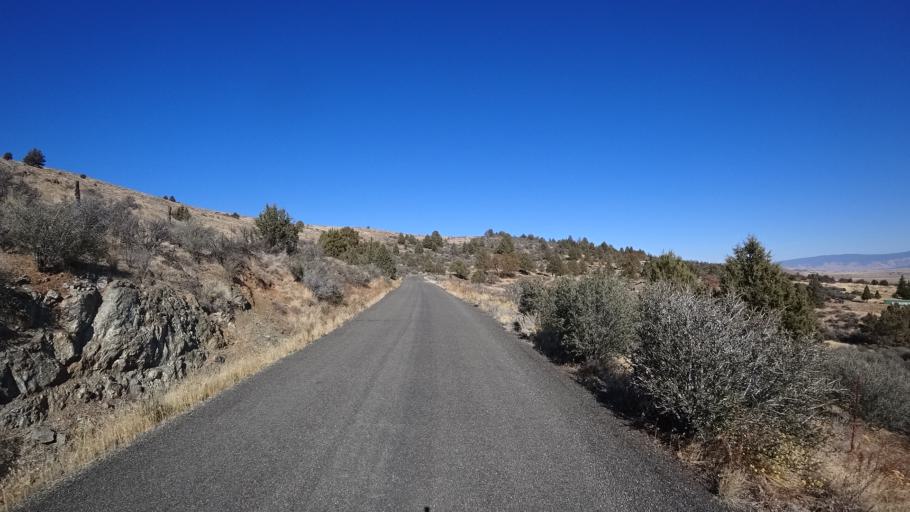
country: US
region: California
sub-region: Siskiyou County
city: Yreka
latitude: 41.7442
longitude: -122.6123
